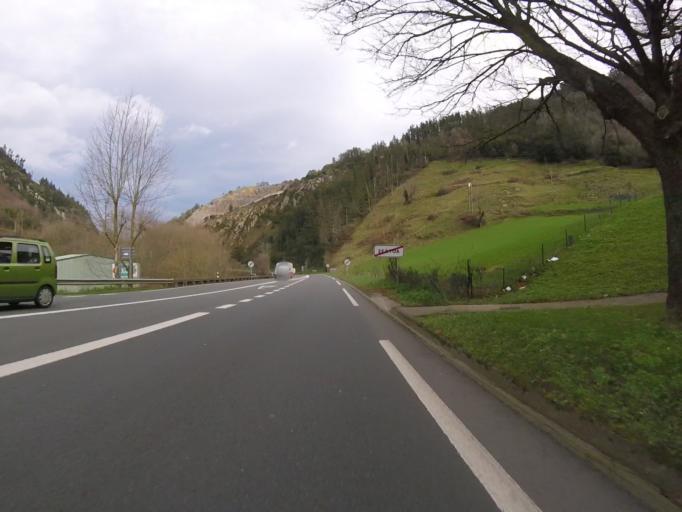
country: ES
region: Basque Country
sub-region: Provincia de Guipuzcoa
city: Cestona
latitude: 43.2424
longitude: -2.2589
